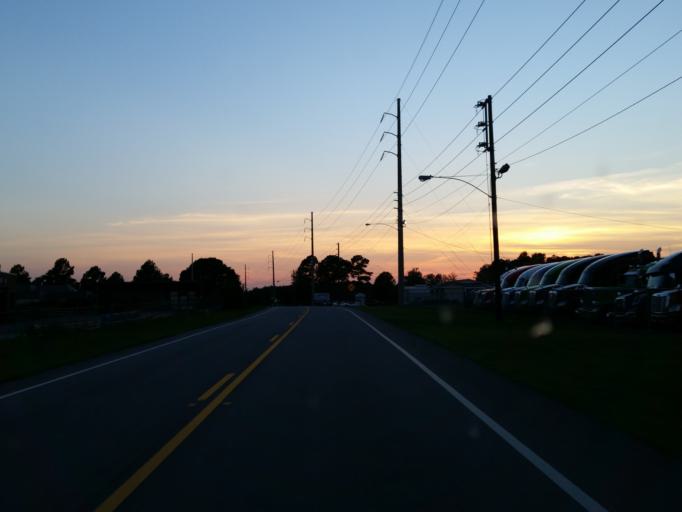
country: US
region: Georgia
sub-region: Tift County
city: Unionville
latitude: 31.4172
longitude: -83.4955
